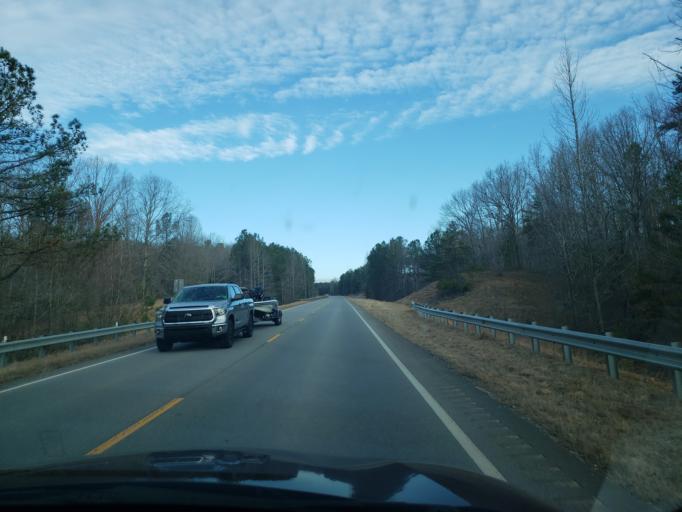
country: US
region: Alabama
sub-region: Randolph County
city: Wedowee
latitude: 33.4322
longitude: -85.5561
